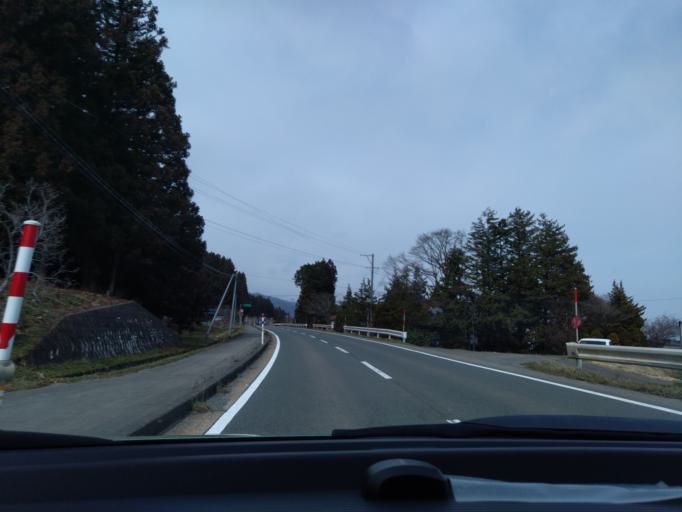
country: JP
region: Iwate
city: Hanamaki
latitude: 39.5370
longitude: 141.1109
